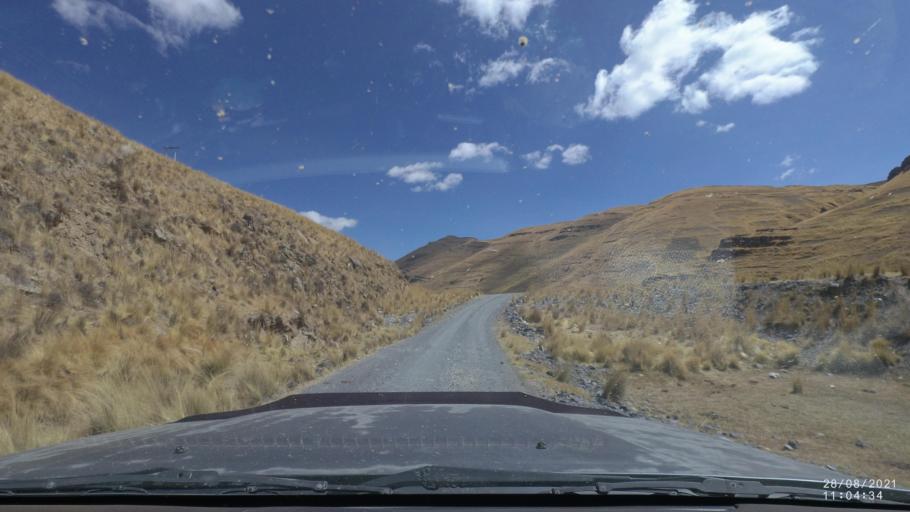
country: BO
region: Cochabamba
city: Cochabamba
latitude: -17.1739
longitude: -66.2831
